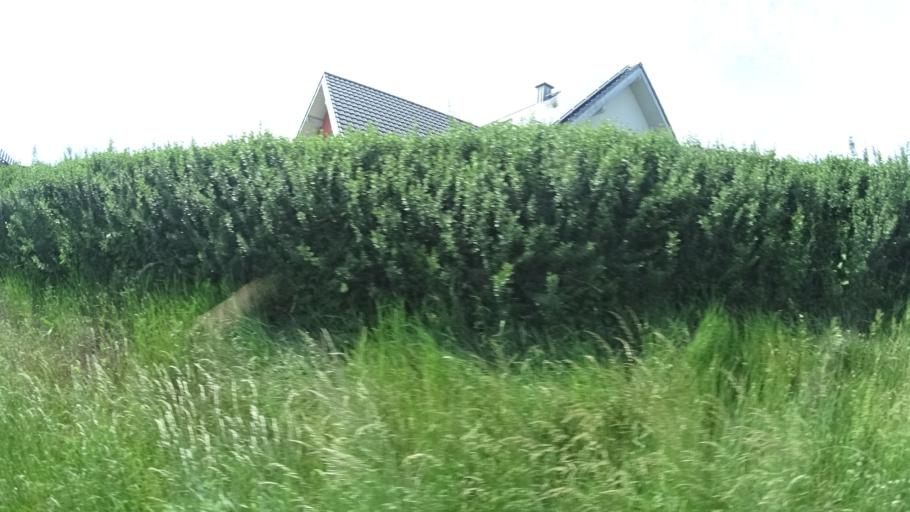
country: DE
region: Bavaria
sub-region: Regierungsbezirk Unterfranken
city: Birkenfeld
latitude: 49.8617
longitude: 9.7054
